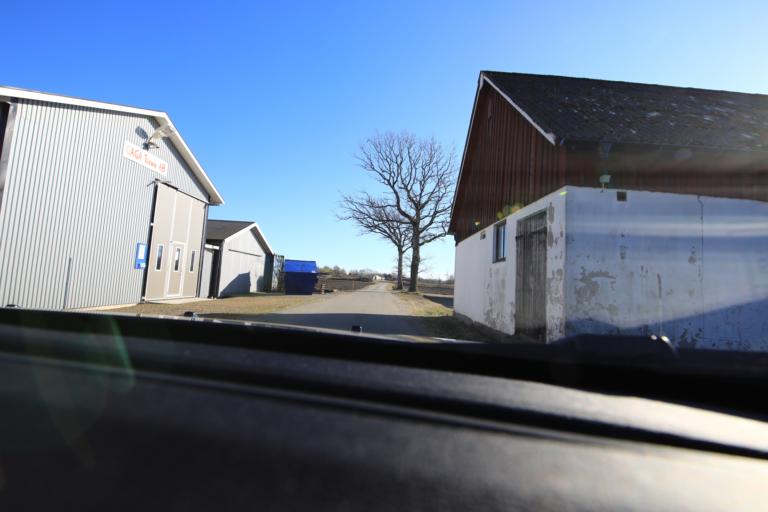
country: SE
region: Halland
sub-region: Varbergs Kommun
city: Tvaaker
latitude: 57.0567
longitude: 12.3726
